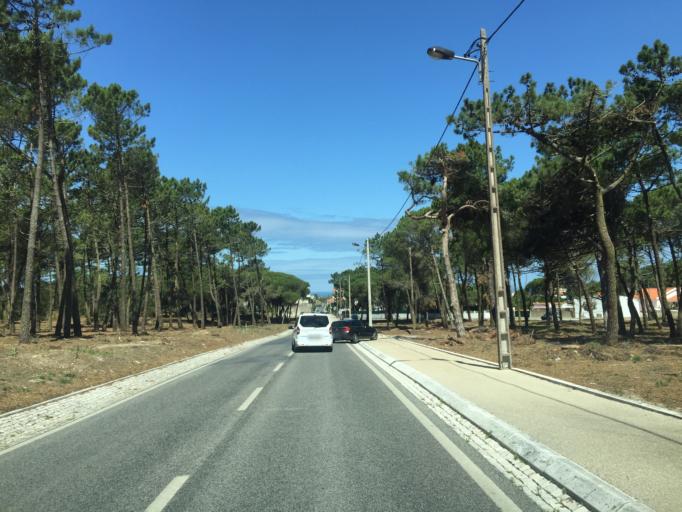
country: PT
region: Lisbon
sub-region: Sintra
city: Colares
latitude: 38.8343
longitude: -9.4552
